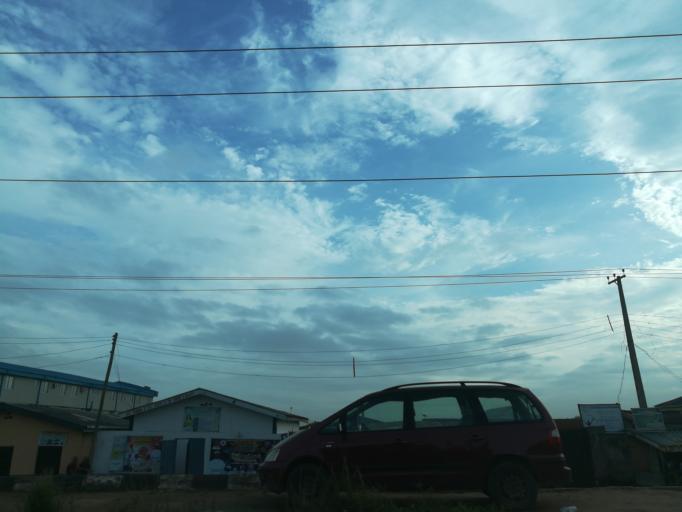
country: NG
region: Lagos
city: Ebute Ikorodu
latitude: 6.6140
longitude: 3.4770
